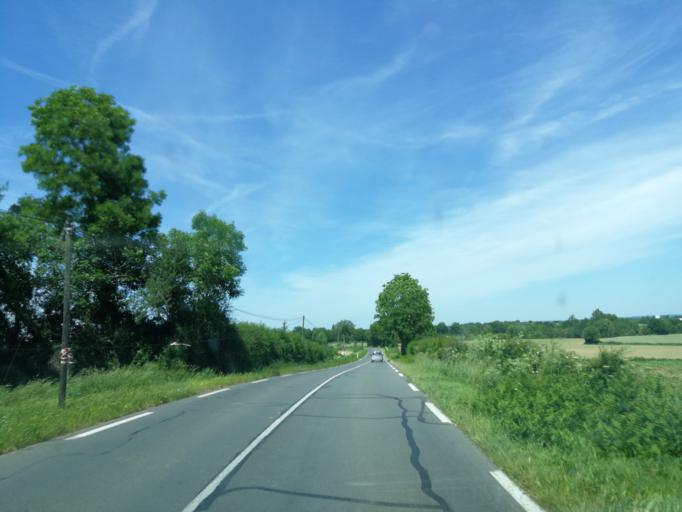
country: FR
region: Pays de la Loire
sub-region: Departement de la Vendee
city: Saint-Pierre-du-Chemin
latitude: 46.7122
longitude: -0.6835
